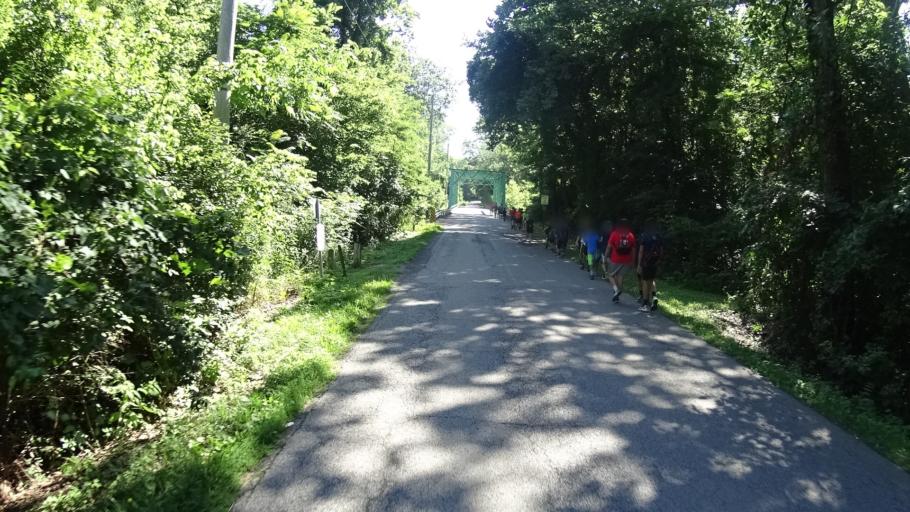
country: US
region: Indiana
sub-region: Madison County
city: Pendleton
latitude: 40.0078
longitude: -85.7363
